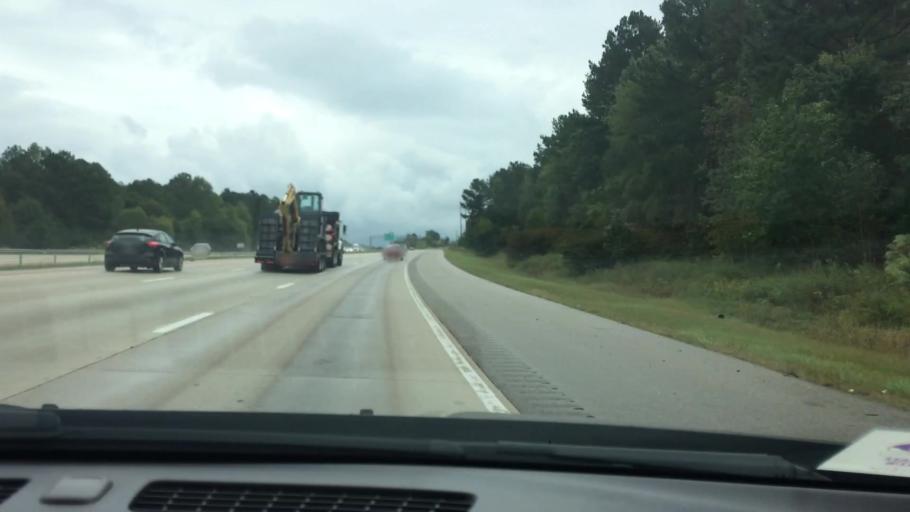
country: US
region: North Carolina
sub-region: Wake County
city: Knightdale
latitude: 35.7714
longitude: -78.5320
